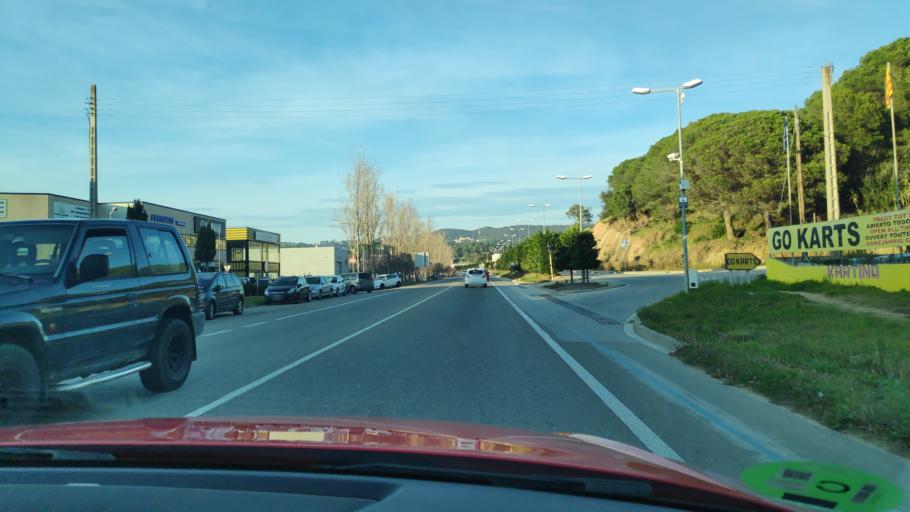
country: ES
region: Catalonia
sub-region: Provincia de Girona
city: Lloret de Mar
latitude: 41.7108
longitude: 2.8320
